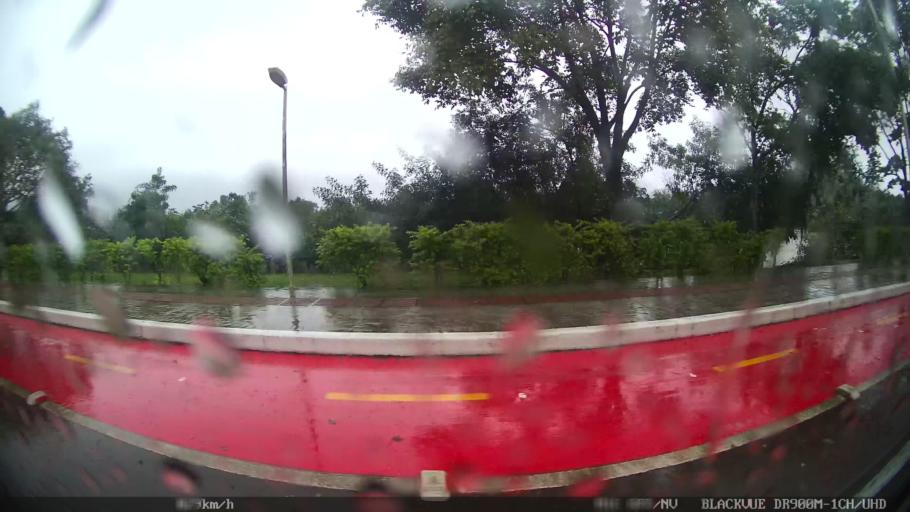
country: BR
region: Santa Catarina
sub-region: Balneario Camboriu
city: Balneario Camboriu
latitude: -27.0061
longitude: -48.6153
